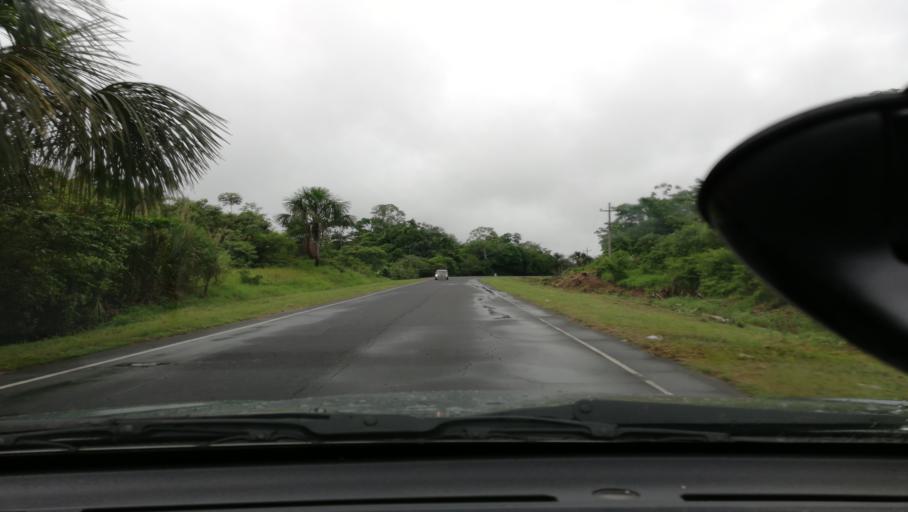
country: PE
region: Loreto
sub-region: Provincia de Maynas
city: San Juan
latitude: -4.0359
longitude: -73.4363
